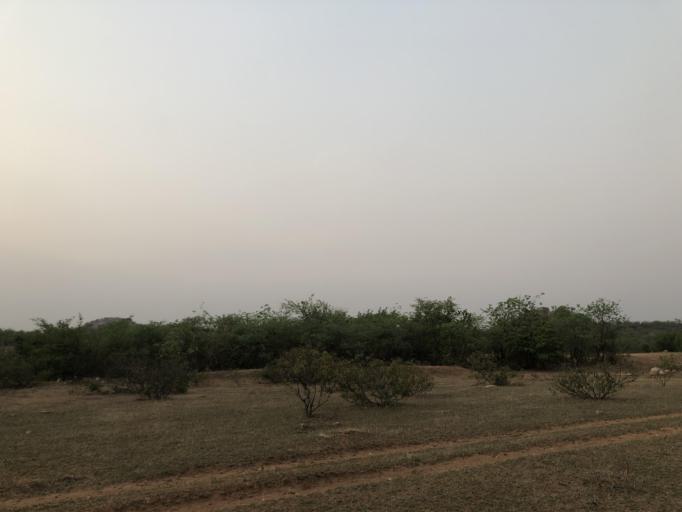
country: IN
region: Telangana
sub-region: Mahbubnagar
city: Farrukhnagar
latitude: 16.8955
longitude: 78.5014
